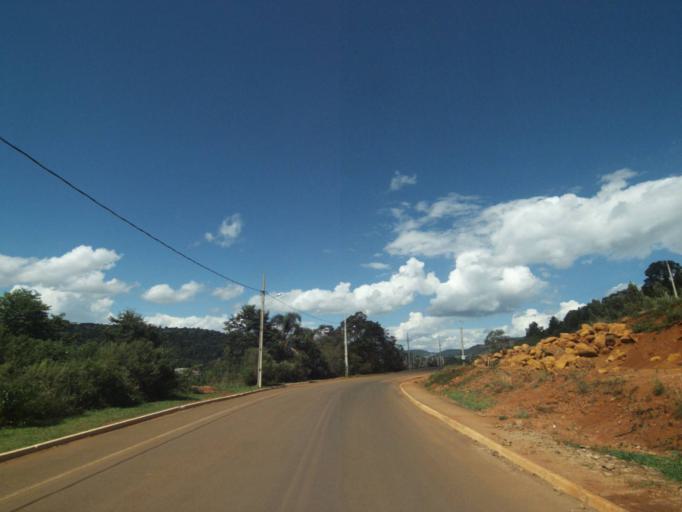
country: BR
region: Parana
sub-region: Uniao Da Vitoria
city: Uniao da Vitoria
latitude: -26.1545
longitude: -51.5508
